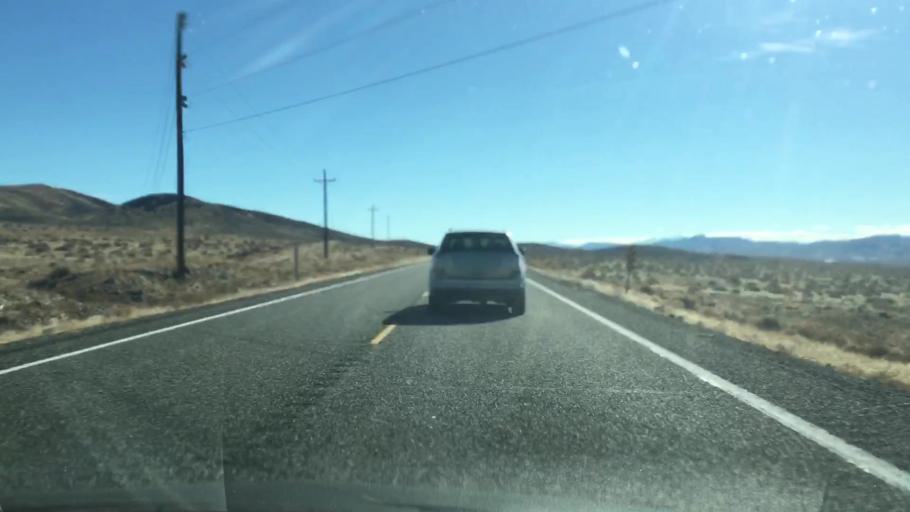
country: US
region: Nevada
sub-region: Lyon County
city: Yerington
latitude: 39.1968
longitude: -119.2128
